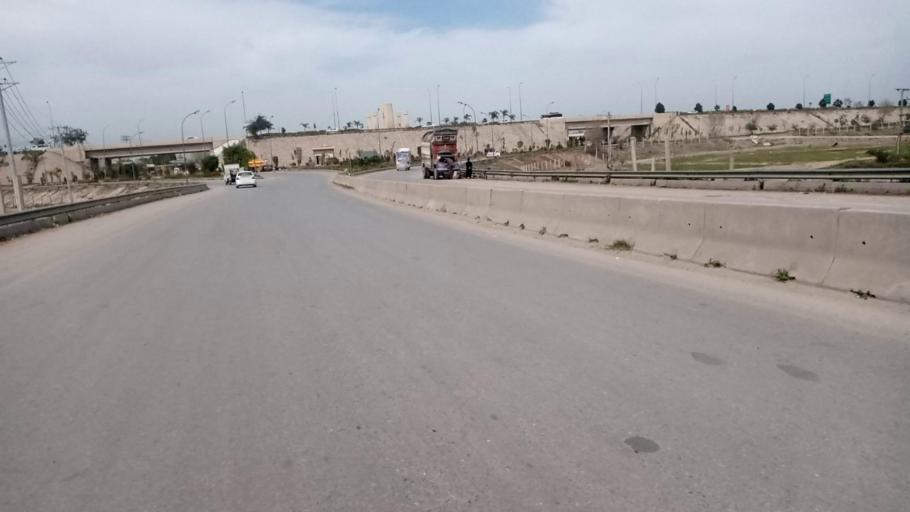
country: PK
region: Khyber Pakhtunkhwa
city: Peshawar
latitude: 34.0244
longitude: 71.6444
